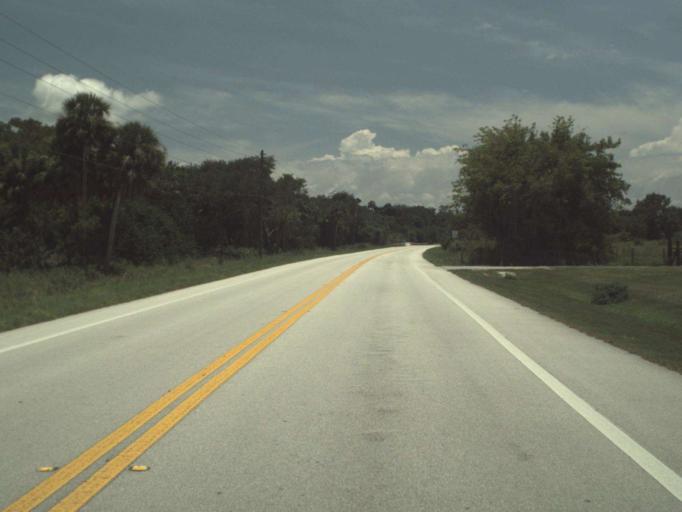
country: US
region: Florida
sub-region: Okeechobee County
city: Taylor Creek
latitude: 27.1128
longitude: -80.6658
